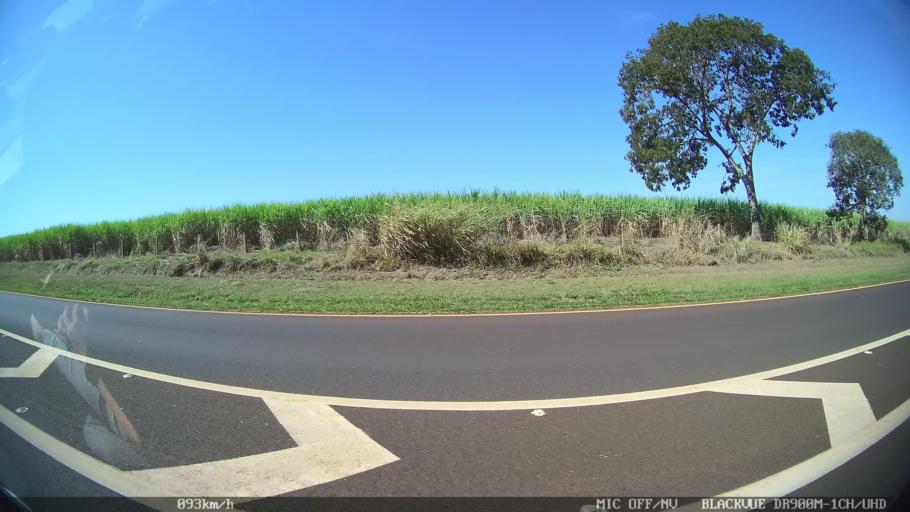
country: BR
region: Sao Paulo
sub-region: Batatais
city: Batatais
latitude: -20.8312
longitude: -47.5989
